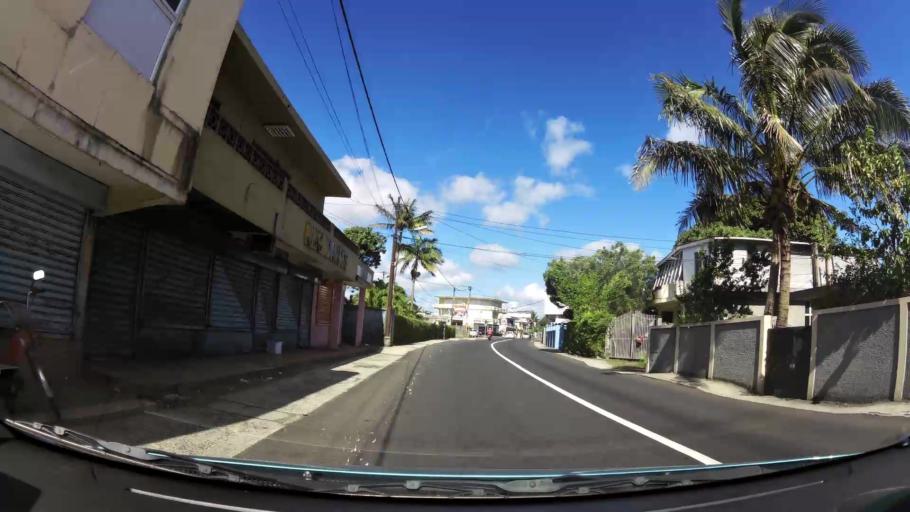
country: MU
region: Plaines Wilhems
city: Vacoas
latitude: -20.3049
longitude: 57.4923
